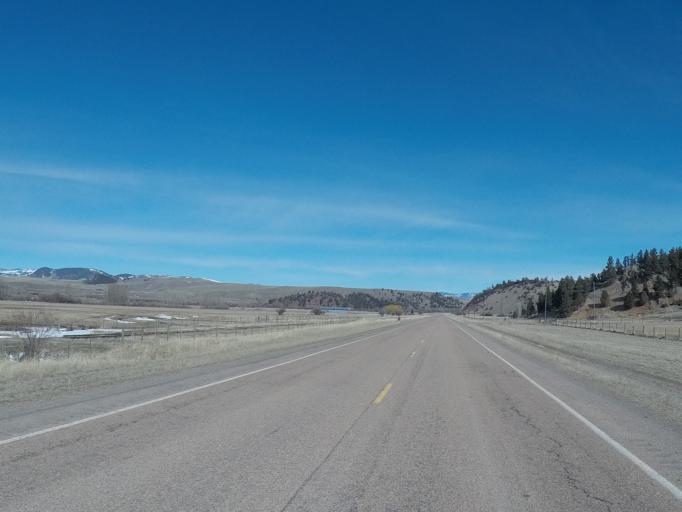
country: US
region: Montana
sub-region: Granite County
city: Philipsburg
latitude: 46.4994
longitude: -113.2231
